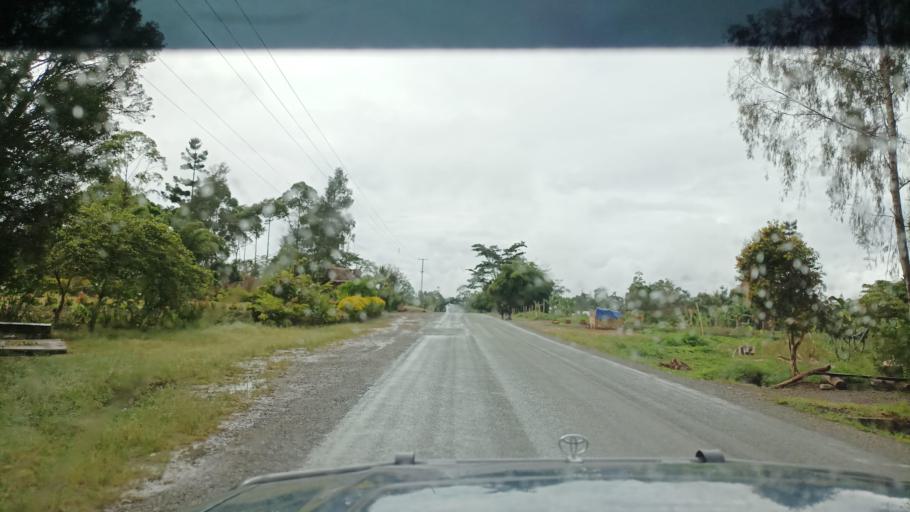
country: PG
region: Jiwaka
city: Minj
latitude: -5.8766
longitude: 144.6695
